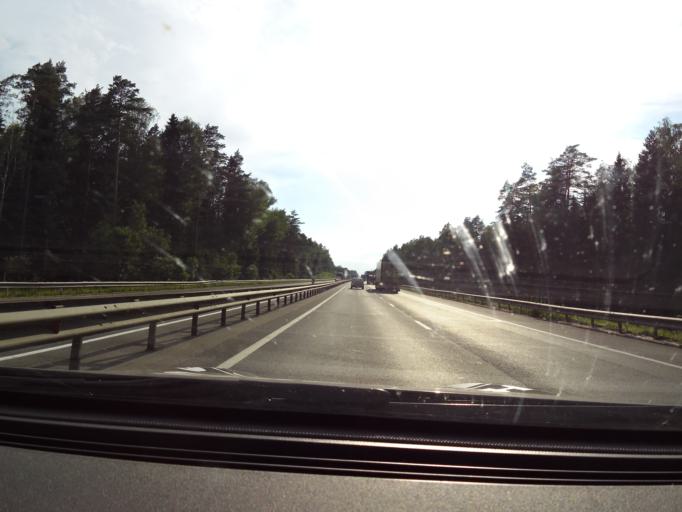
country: RU
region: Vladimir
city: Stepantsevo
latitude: 56.2300
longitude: 41.7216
